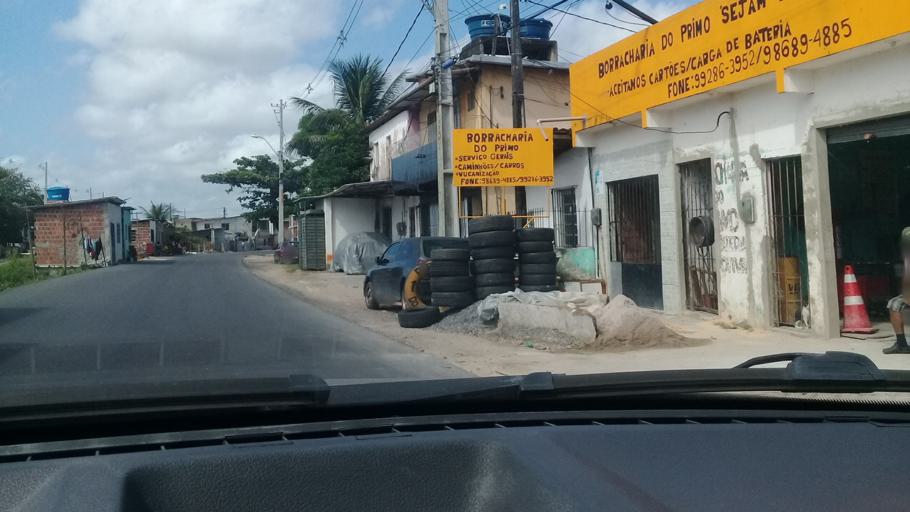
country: BR
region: Pernambuco
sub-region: Recife
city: Recife
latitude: -8.0685
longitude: -34.9386
